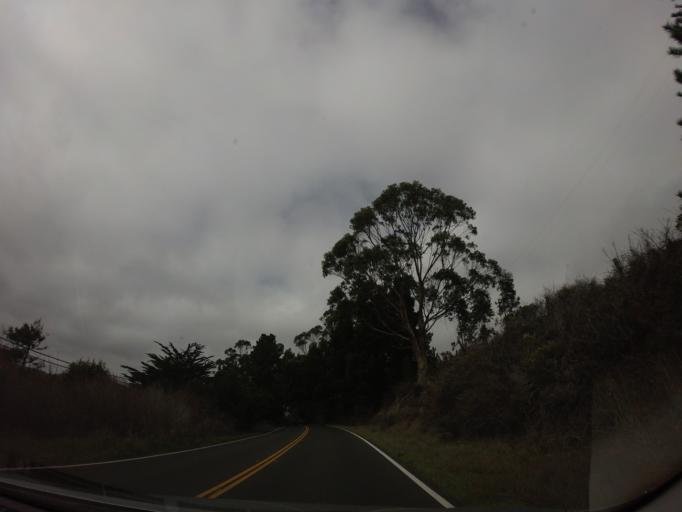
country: US
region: California
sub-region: Marin County
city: Inverness
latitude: 38.1319
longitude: -122.8681
